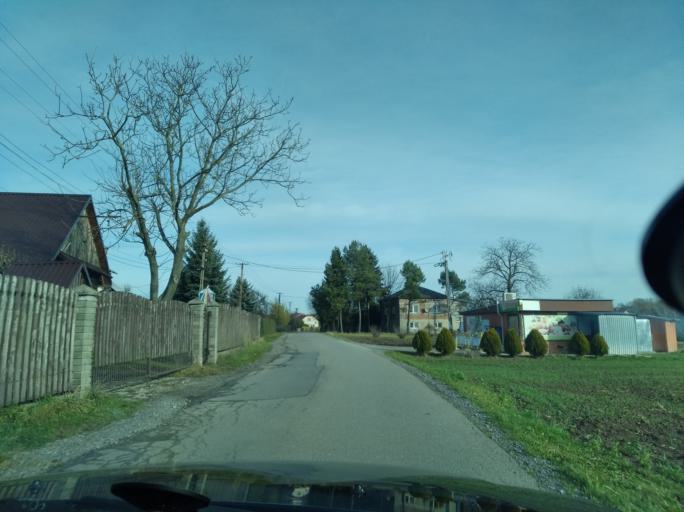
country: PL
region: Subcarpathian Voivodeship
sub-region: Powiat rzeszowski
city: Krasne
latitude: 50.0107
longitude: 22.0949
